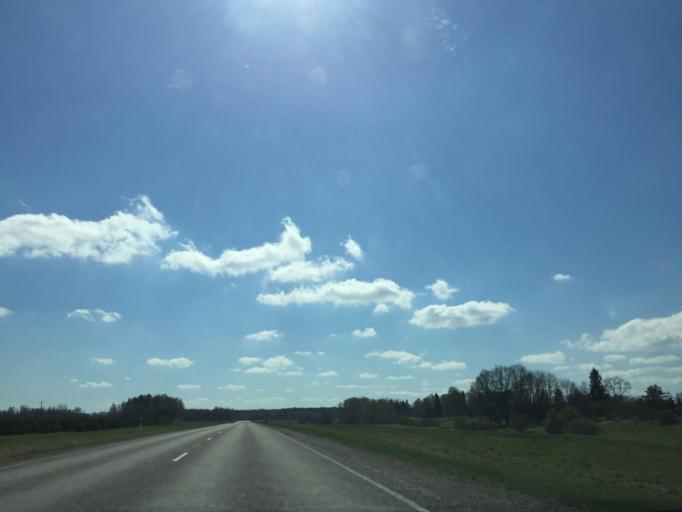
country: EE
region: Valgamaa
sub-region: Torva linn
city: Torva
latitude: 58.0280
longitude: 26.1722
